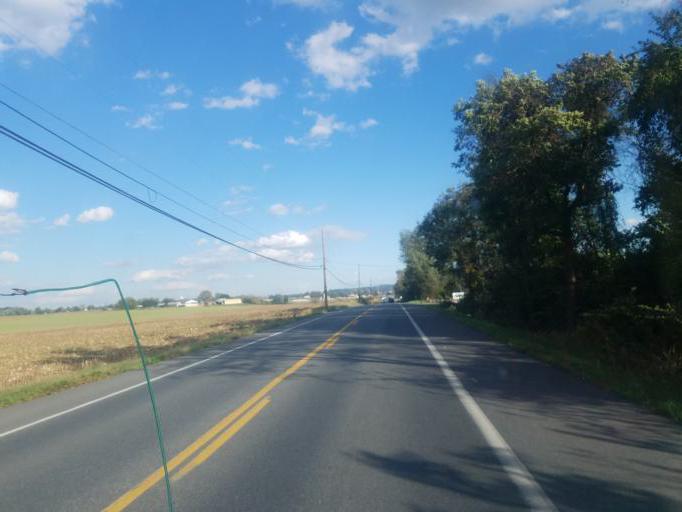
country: US
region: Pennsylvania
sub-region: Lancaster County
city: Maytown
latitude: 40.0652
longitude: -76.5921
